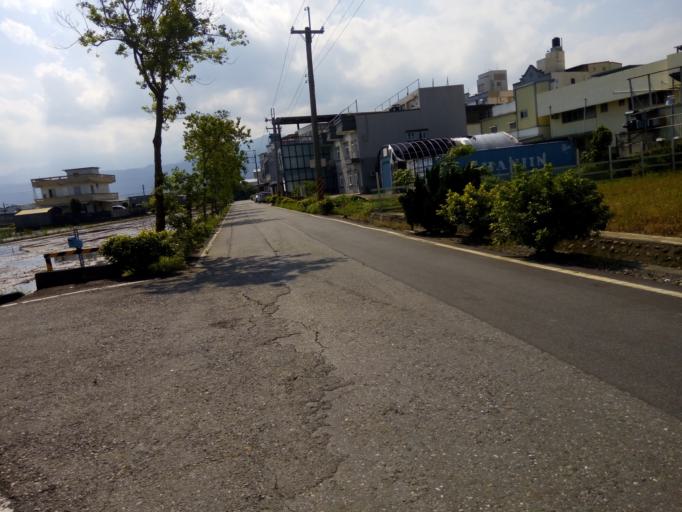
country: TW
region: Taiwan
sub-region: Yilan
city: Yilan
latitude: 24.6705
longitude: 121.7786
